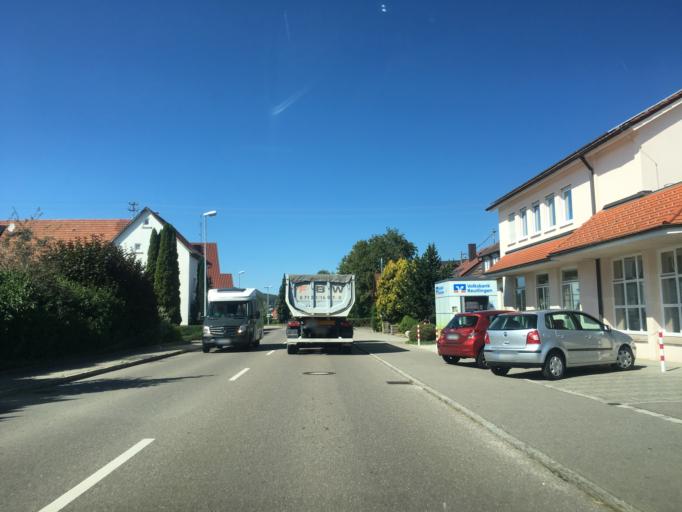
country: DE
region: Baden-Wuerttemberg
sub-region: Tuebingen Region
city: Sankt Johann
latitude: 48.3874
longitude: 9.2949
